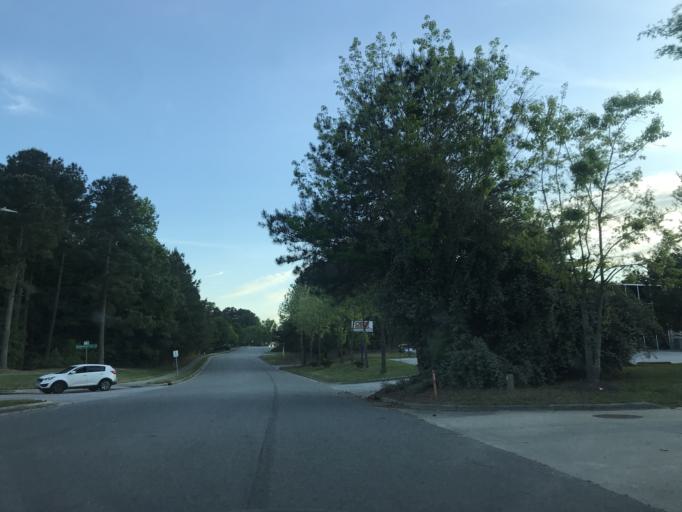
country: US
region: North Carolina
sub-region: Wake County
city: Knightdale
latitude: 35.7651
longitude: -78.5535
